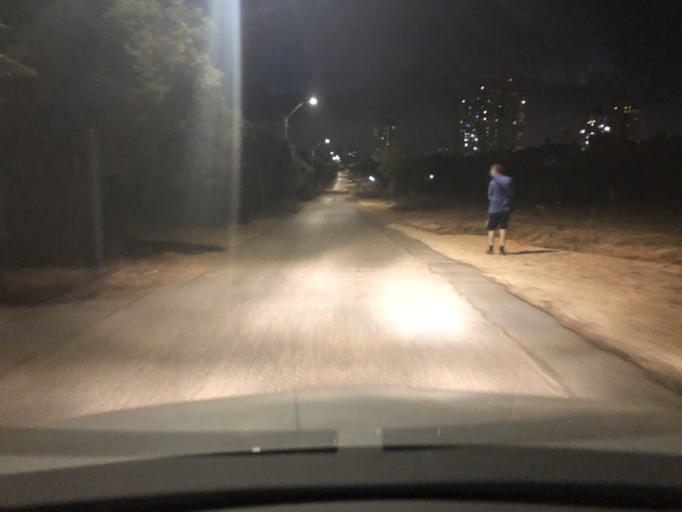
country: IL
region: Central District
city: Hod HaSharon
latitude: 32.1673
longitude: 34.8963
